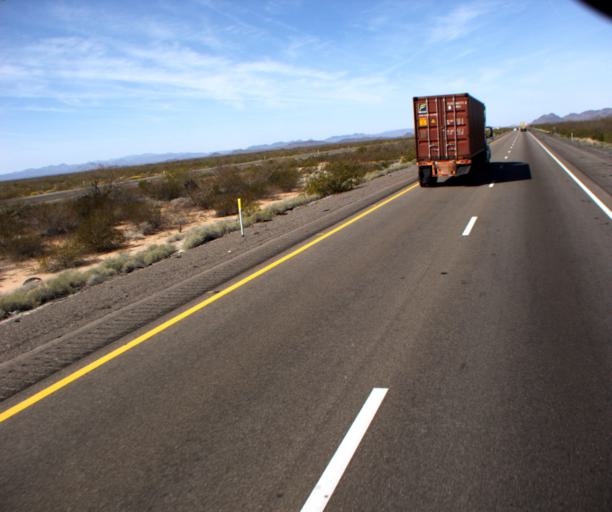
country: US
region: Arizona
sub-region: La Paz County
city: Salome
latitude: 33.5911
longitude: -113.4979
